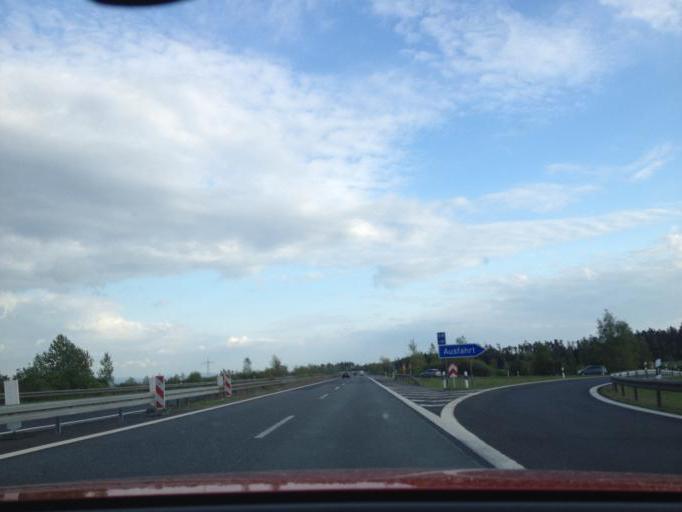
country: DE
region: Bavaria
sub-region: Upper Palatinate
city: Mitterteich
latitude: 49.9378
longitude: 12.2244
